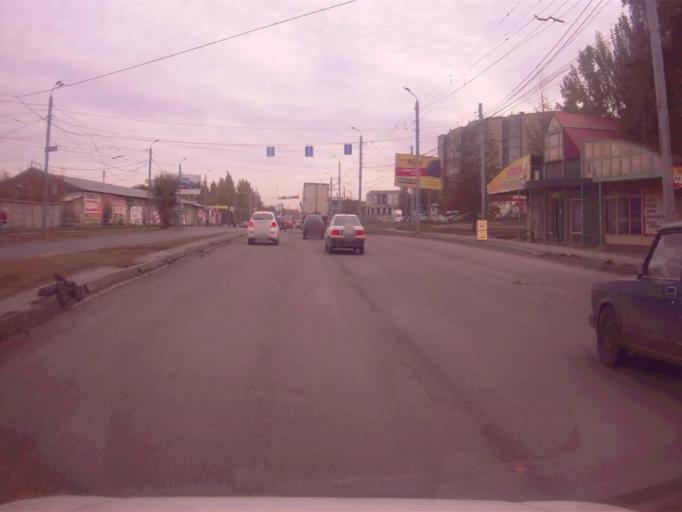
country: RU
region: Chelyabinsk
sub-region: Gorod Chelyabinsk
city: Chelyabinsk
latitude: 55.1430
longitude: 61.4511
